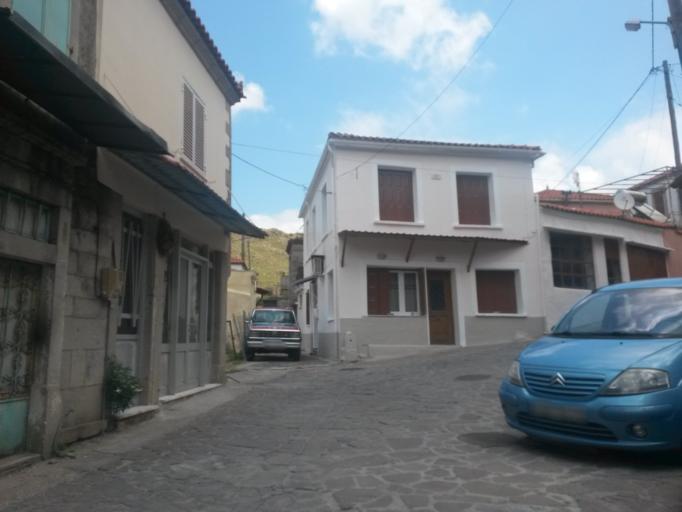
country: GR
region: North Aegean
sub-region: Nomos Lesvou
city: Petra
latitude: 39.2606
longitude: 26.0748
